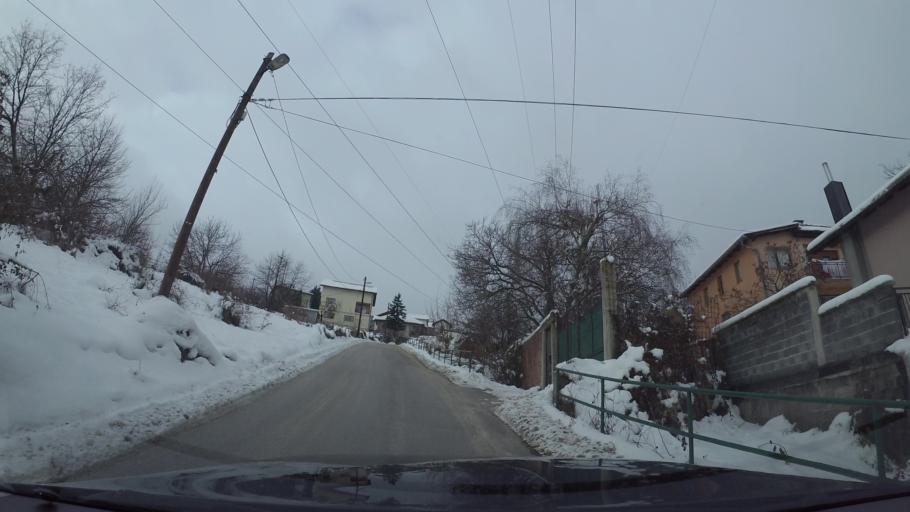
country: BA
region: Federation of Bosnia and Herzegovina
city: Kobilja Glava
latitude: 43.8661
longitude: 18.3967
